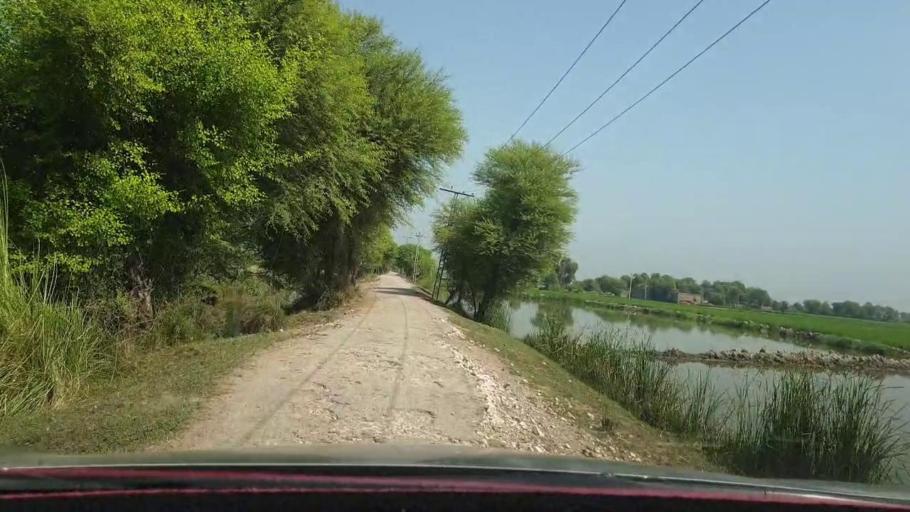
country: PK
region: Sindh
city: Warah
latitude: 27.4951
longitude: 67.8357
